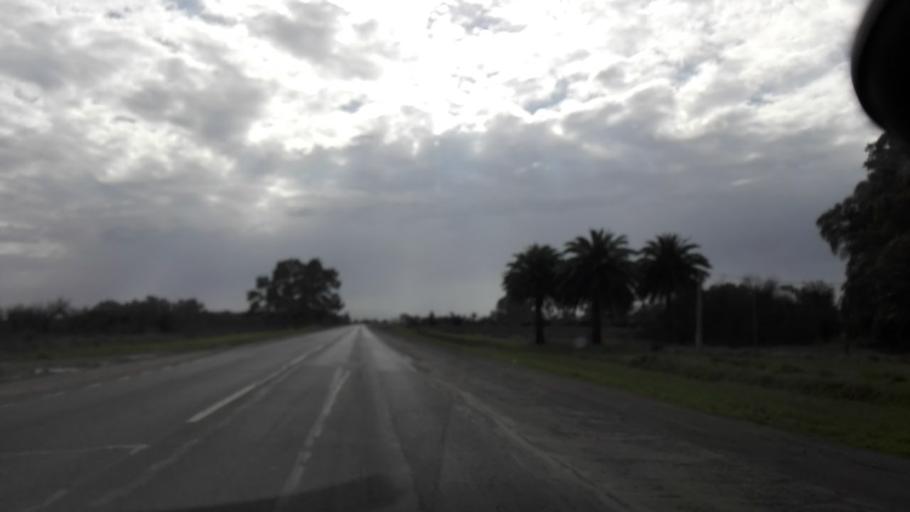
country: AR
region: Buenos Aires
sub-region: Partido de Las Flores
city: Las Flores
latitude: -36.0064
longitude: -59.0654
